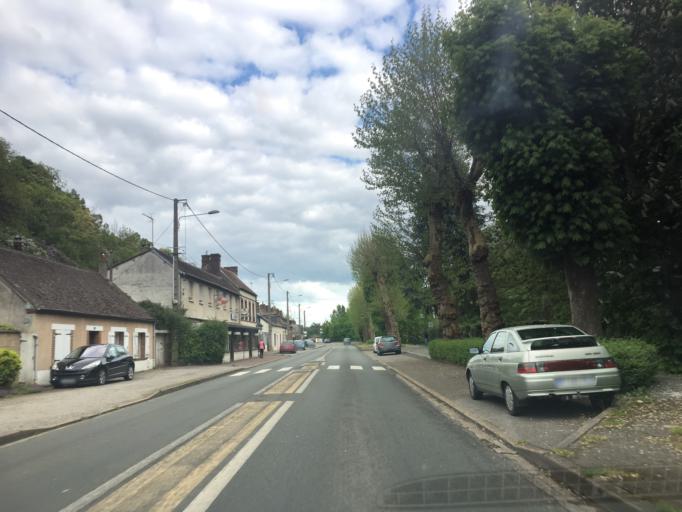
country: FR
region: Centre
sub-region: Departement d'Eure-et-Loir
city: Saint-Lubin-des-Joncherets
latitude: 48.7665
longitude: 1.2084
